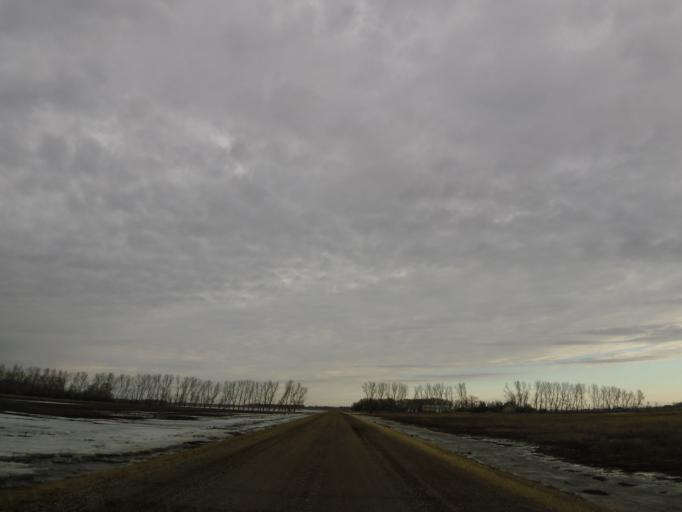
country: US
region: North Dakota
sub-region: Walsh County
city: Grafton
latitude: 48.3989
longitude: -97.4703
